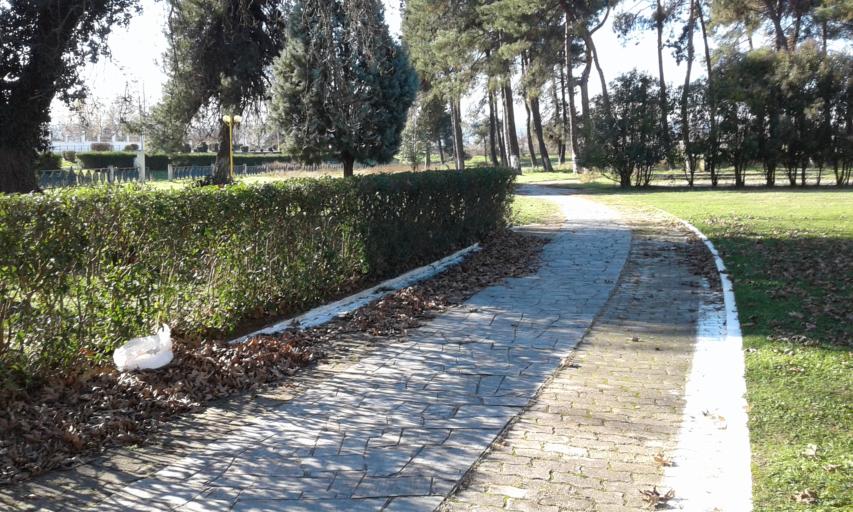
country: GR
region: Central Macedonia
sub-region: Nomos Thessalonikis
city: Lagkadas
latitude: 40.7468
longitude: 23.0609
